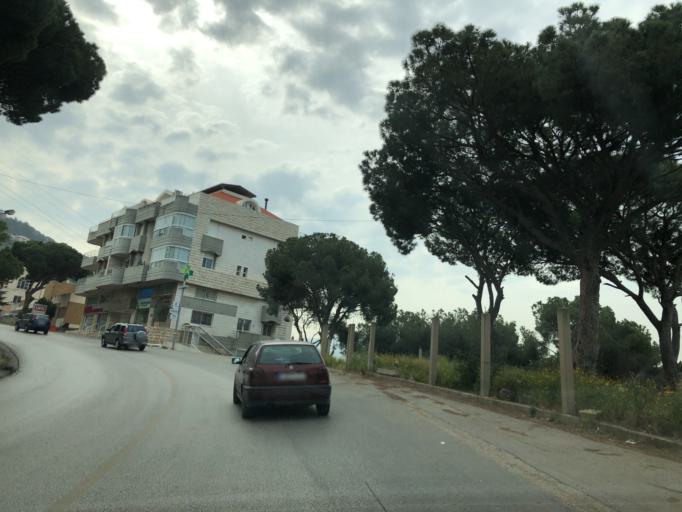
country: LB
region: Mont-Liban
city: Jdaidet el Matn
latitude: 33.8552
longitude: 35.5832
